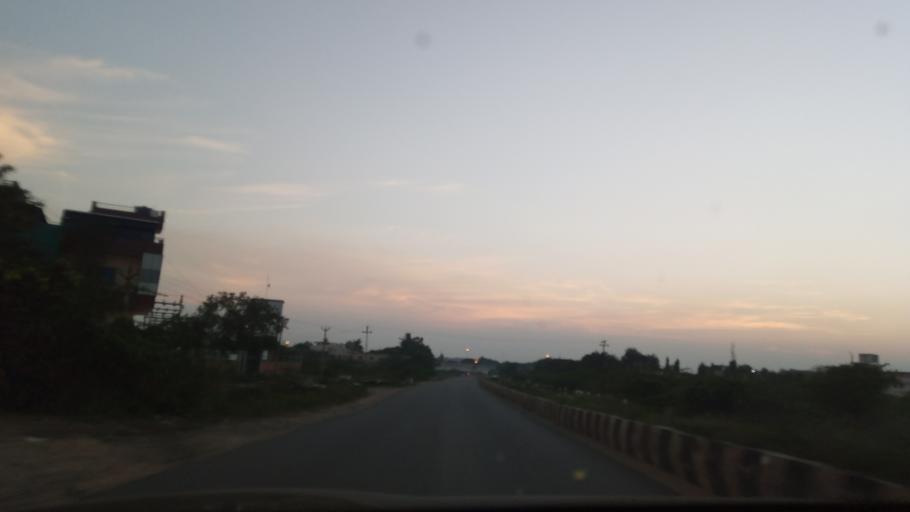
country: IN
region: Tamil Nadu
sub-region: Vellore
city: Walajapet
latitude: 12.9231
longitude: 79.3447
